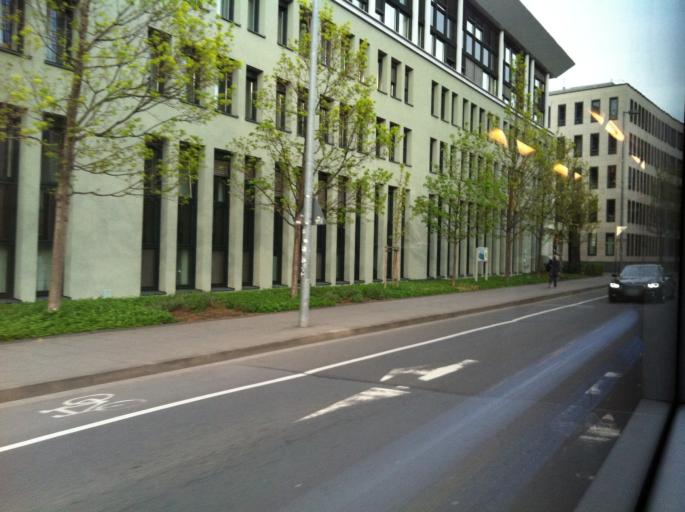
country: DE
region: Rheinland-Pfalz
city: Mainz
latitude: 50.0051
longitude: 8.2668
